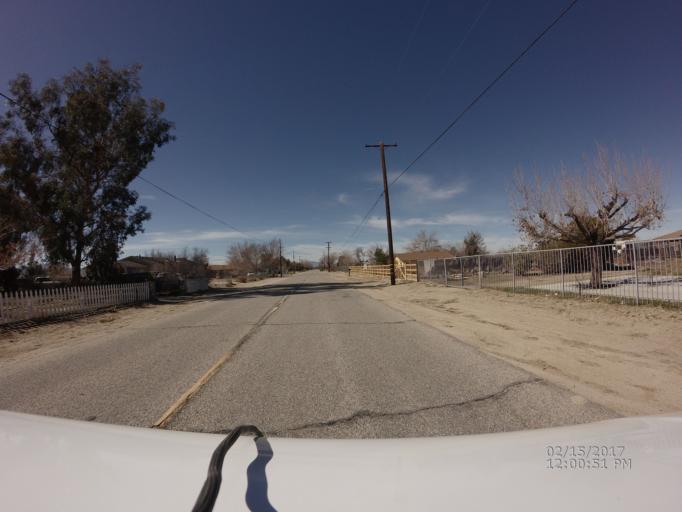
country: US
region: California
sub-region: Los Angeles County
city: Littlerock
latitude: 34.5743
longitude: -117.9488
